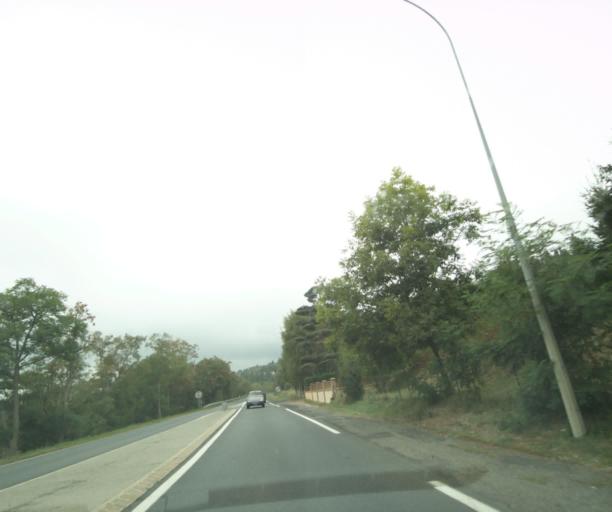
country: FR
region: Auvergne
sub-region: Departement du Puy-de-Dome
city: Saint-Genes-Champanelle
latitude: 45.7056
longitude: 3.0399
